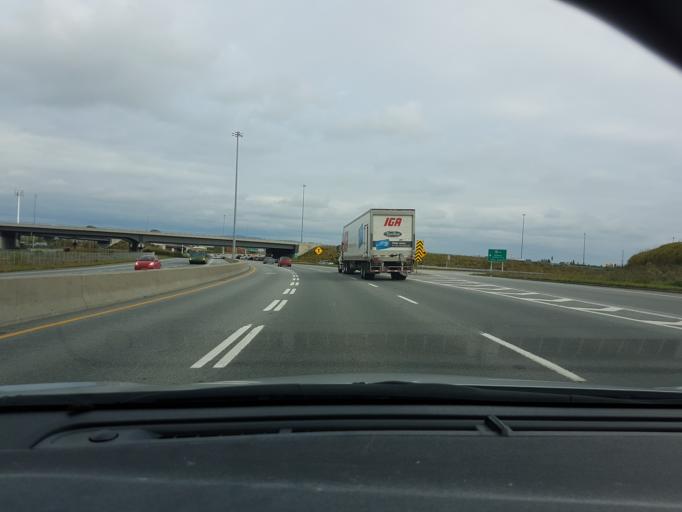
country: CA
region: Quebec
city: L'Ancienne-Lorette
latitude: 46.7920
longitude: -71.2889
